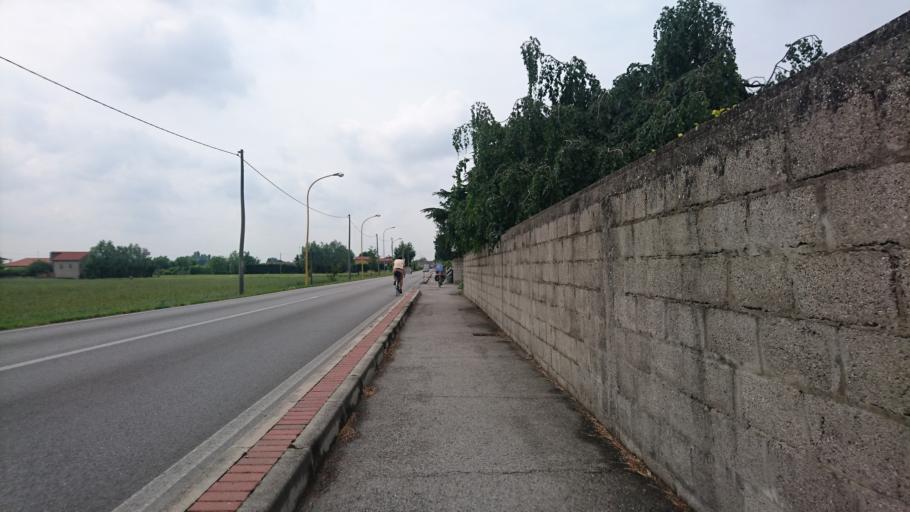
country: IT
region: Veneto
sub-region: Provincia di Padova
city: Villa Estense
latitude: 45.1814
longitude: 11.6713
